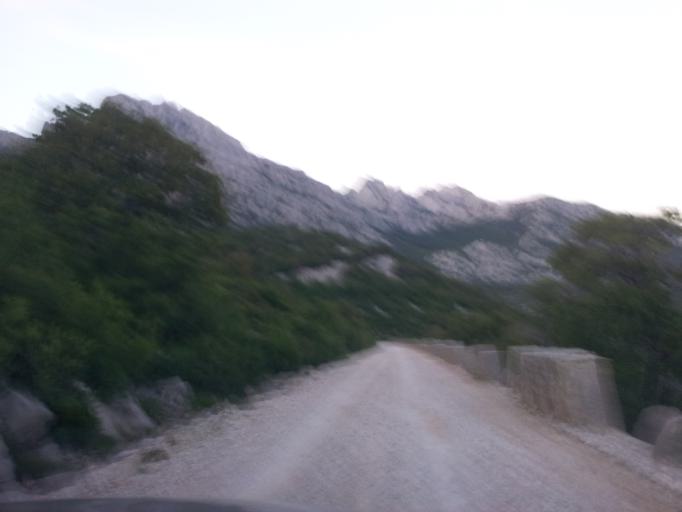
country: HR
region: Zadarska
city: Obrovac
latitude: 44.2537
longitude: 15.6409
